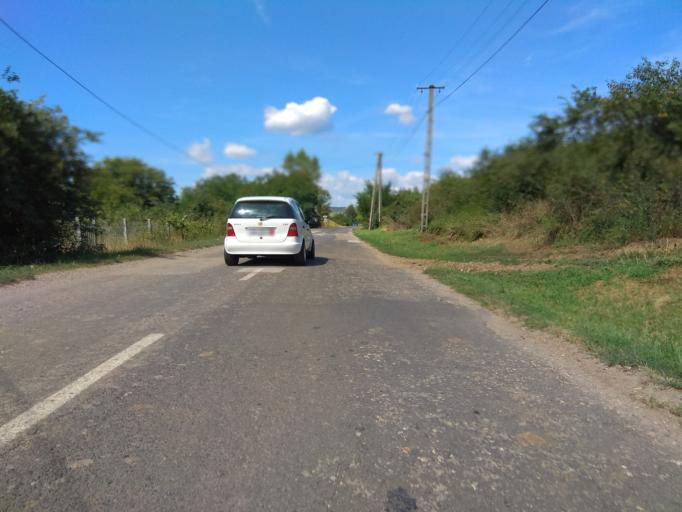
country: HU
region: Borsod-Abauj-Zemplen
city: Izsofalva
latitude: 48.2794
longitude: 20.6446
